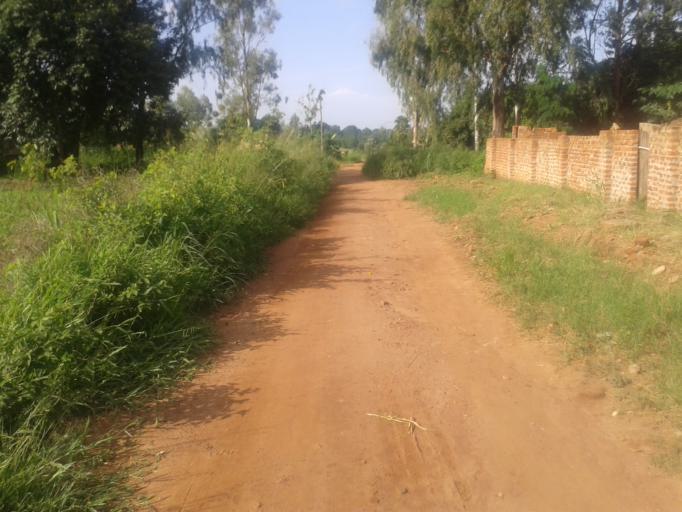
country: UG
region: Northern Region
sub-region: Gulu District
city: Gulu
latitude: 2.7942
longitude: 32.3077
